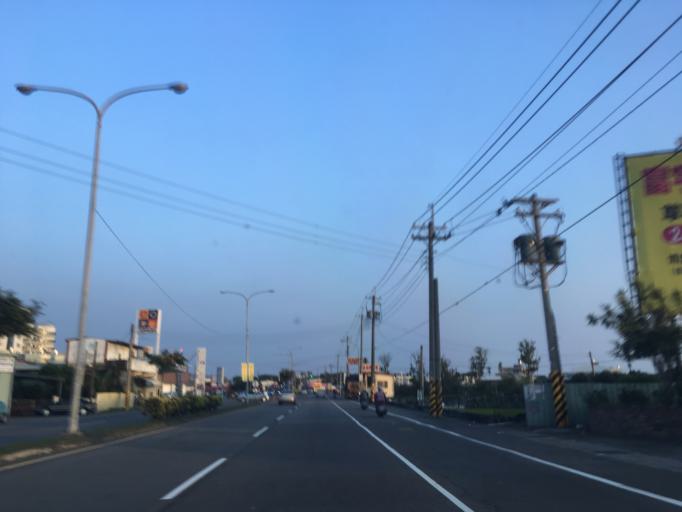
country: TW
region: Taiwan
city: Zhongxing New Village
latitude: 23.9946
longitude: 120.6656
